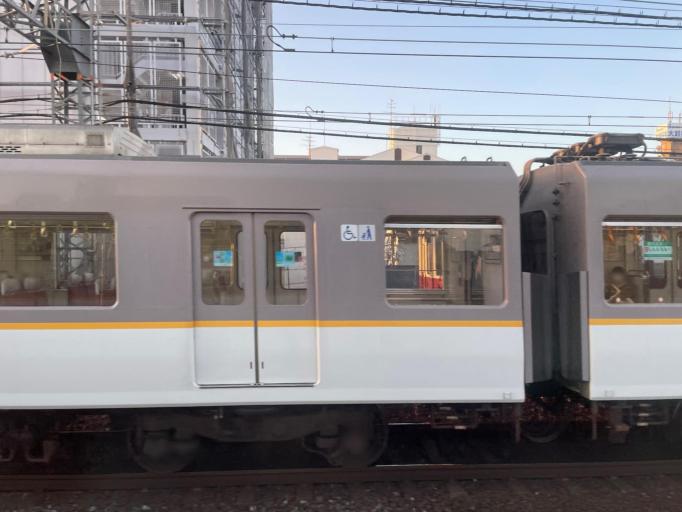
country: JP
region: Osaka
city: Osaka-shi
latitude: 34.6647
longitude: 135.5510
